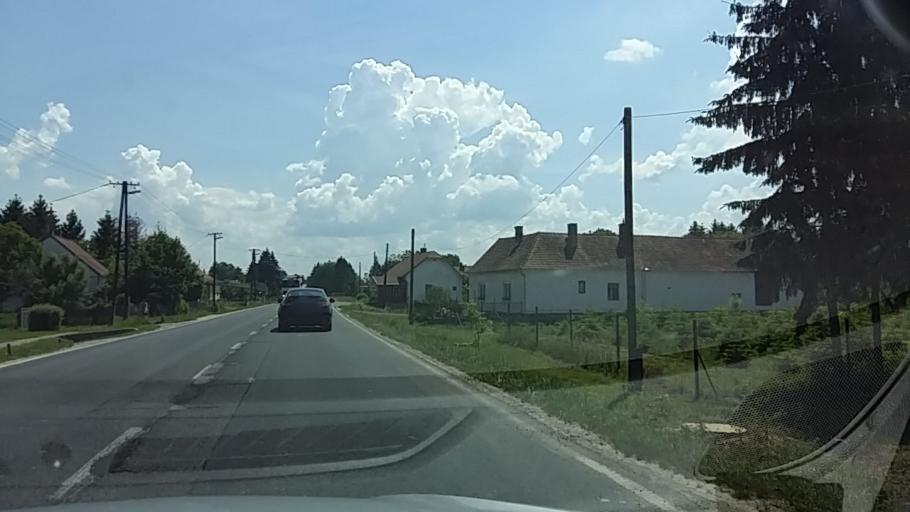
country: AT
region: Burgenland
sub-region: Politischer Bezirk Gussing
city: Heiligenbrunn
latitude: 46.9702
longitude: 16.4013
